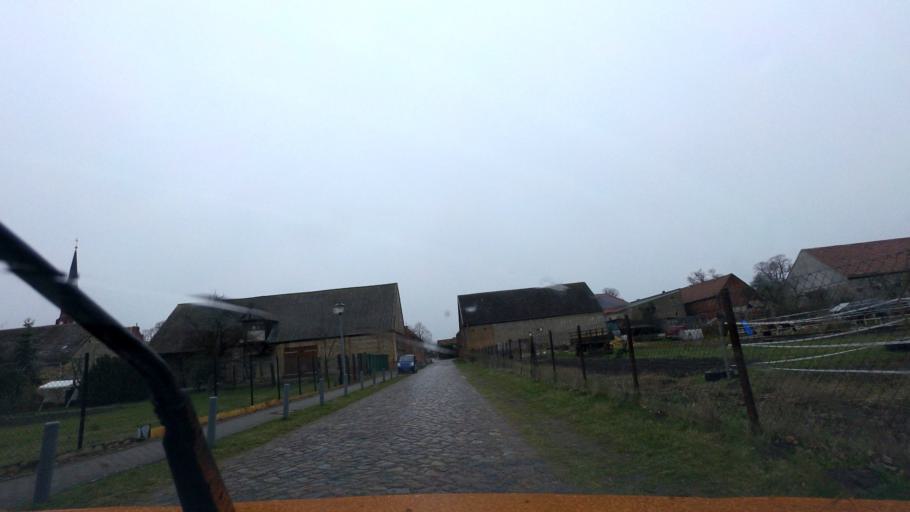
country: DE
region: Brandenburg
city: Brieselang
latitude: 52.6527
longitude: 12.9816
